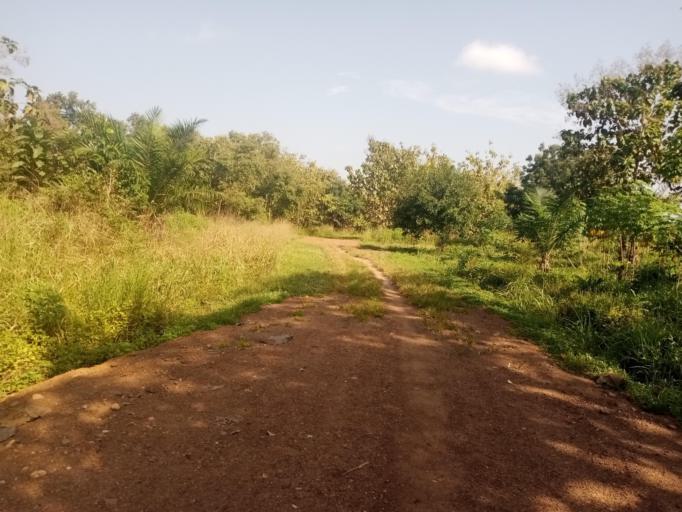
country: TG
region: Maritime
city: Tsevie
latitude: 6.6591
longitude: 0.9722
